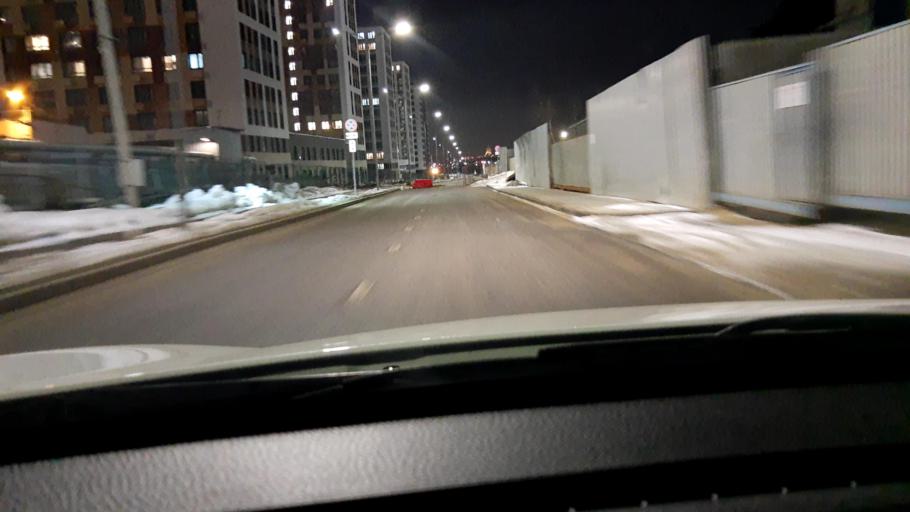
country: RU
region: Moskovskaya
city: Novoivanovskoye
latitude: 55.7004
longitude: 37.3561
